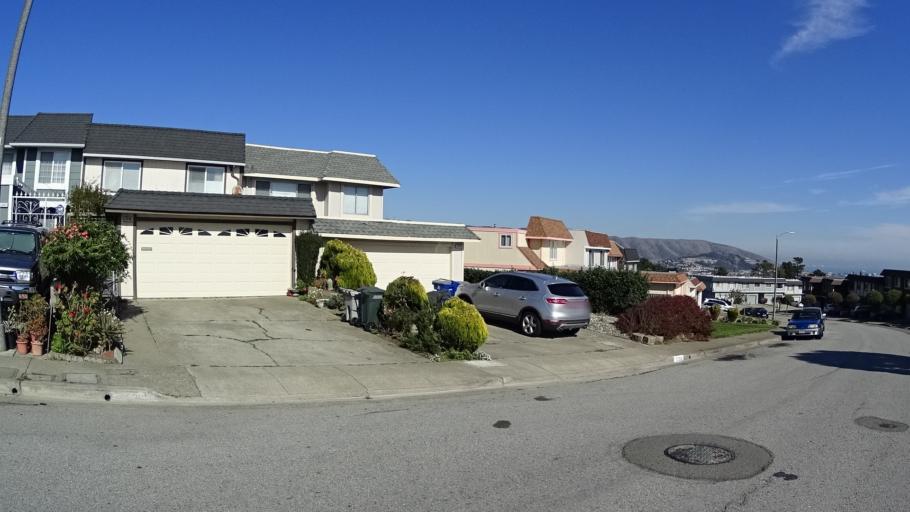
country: US
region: California
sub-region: San Mateo County
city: Colma
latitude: 37.6466
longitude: -122.4585
